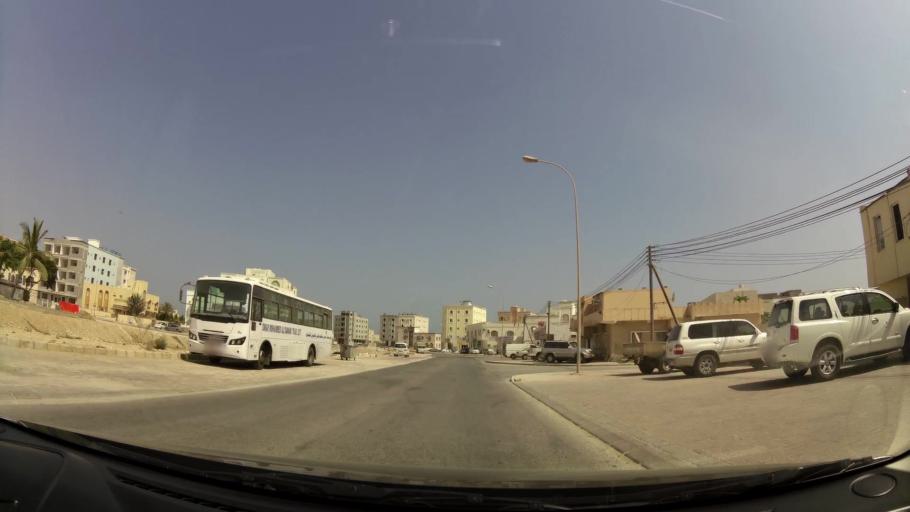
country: OM
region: Zufar
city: Salalah
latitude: 17.0159
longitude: 54.0597
